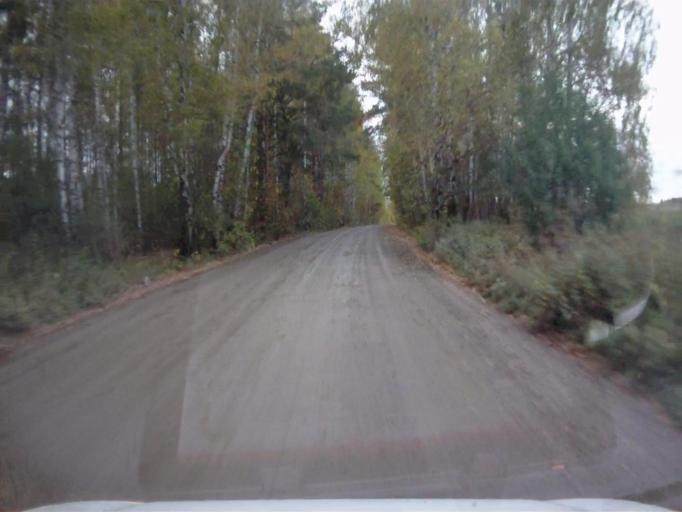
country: RU
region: Sverdlovsk
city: Mikhaylovsk
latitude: 56.1714
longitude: 59.2214
